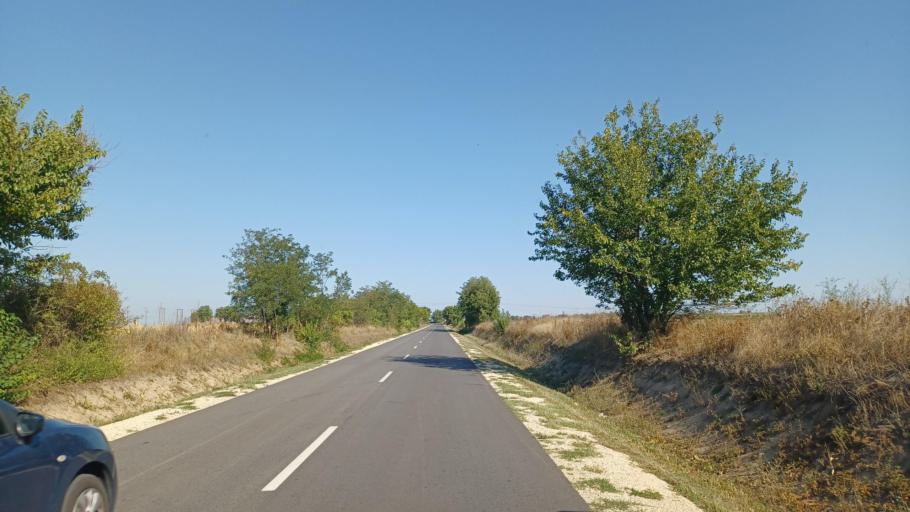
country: HU
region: Tolna
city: Paks
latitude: 46.6429
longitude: 18.8469
